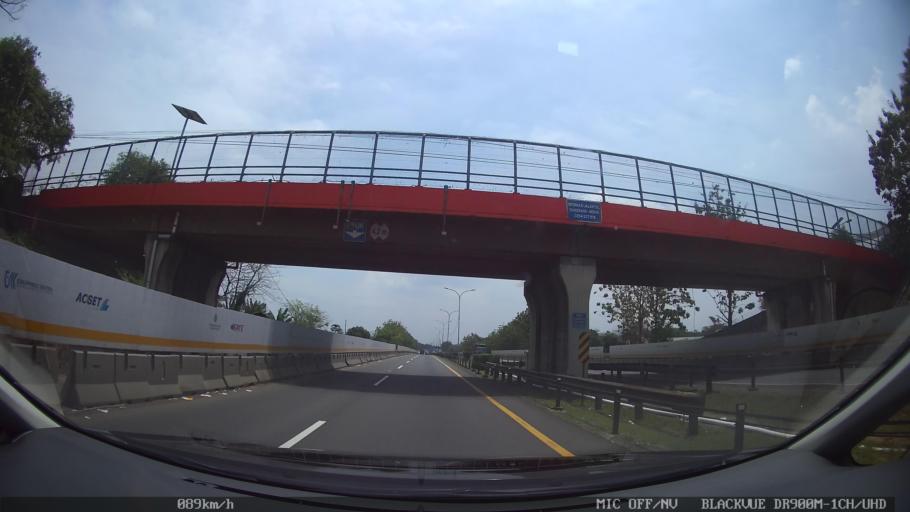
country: ID
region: Banten
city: Serang
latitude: -6.1385
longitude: 106.2300
